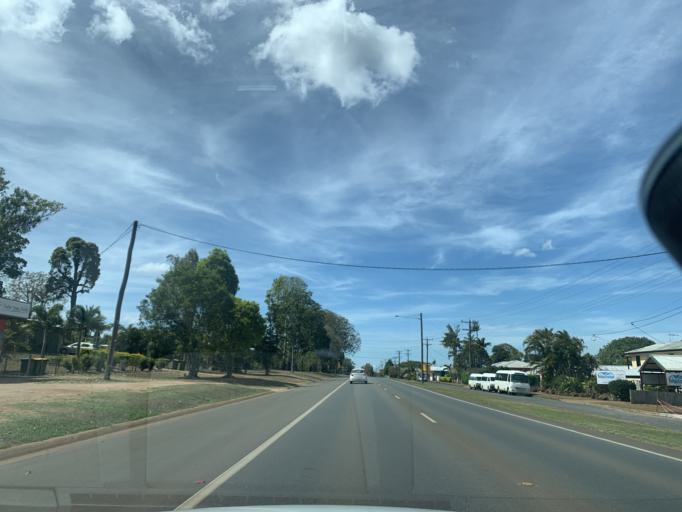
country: AU
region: Queensland
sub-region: Tablelands
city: Tolga
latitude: -17.2264
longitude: 145.4785
